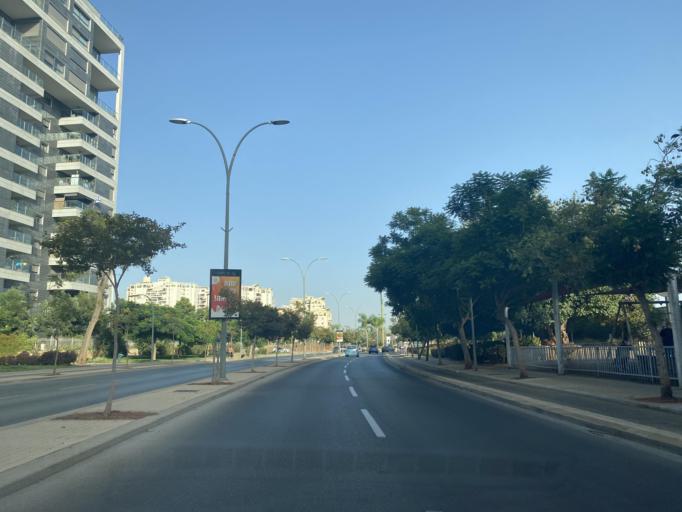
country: IL
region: Central District
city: Kfar Saba
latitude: 32.1645
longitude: 34.9049
